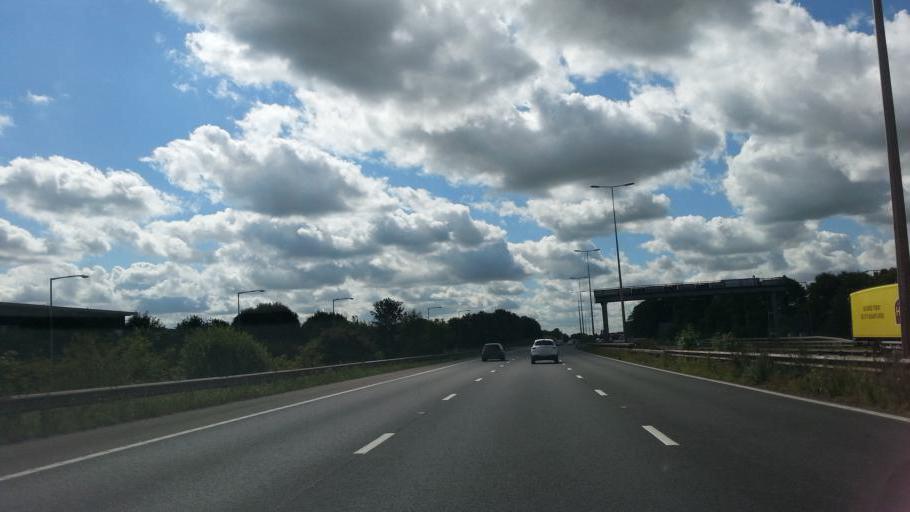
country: GB
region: England
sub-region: Leicestershire
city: Enderby
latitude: 52.5992
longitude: -1.1947
